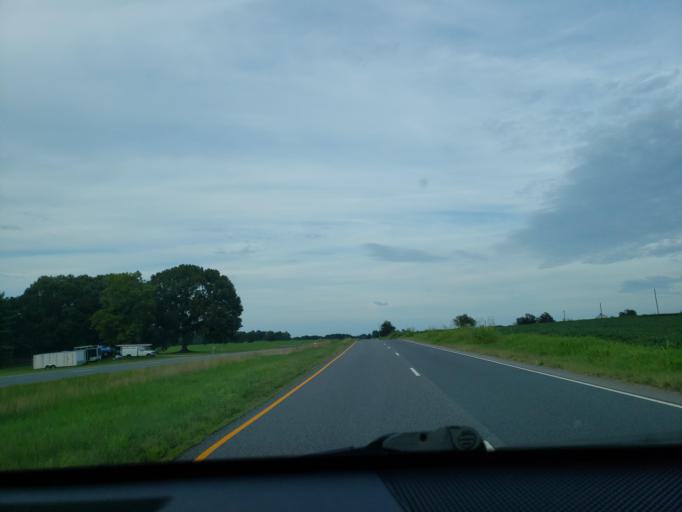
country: US
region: Virginia
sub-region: Brunswick County
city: Lawrenceville
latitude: 36.7180
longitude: -77.9698
